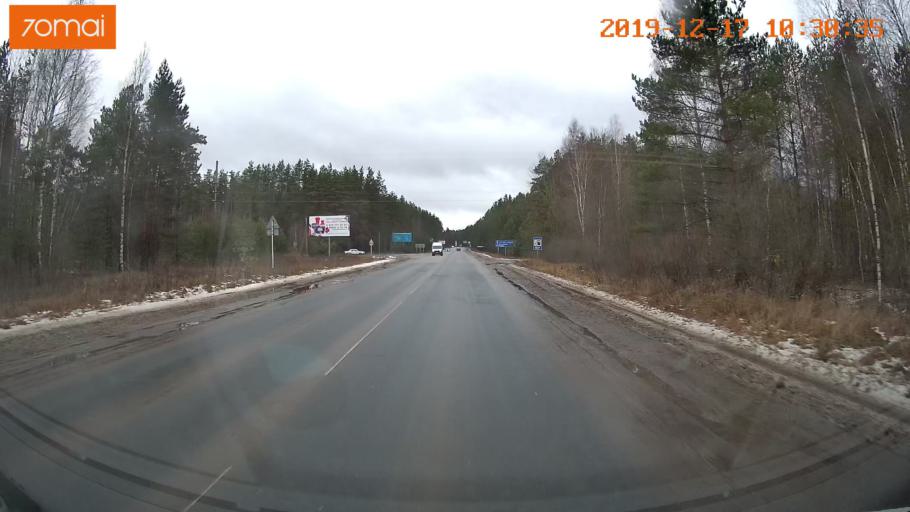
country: RU
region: Vladimir
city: Gus'-Khrustal'nyy
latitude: 55.6418
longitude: 40.7072
